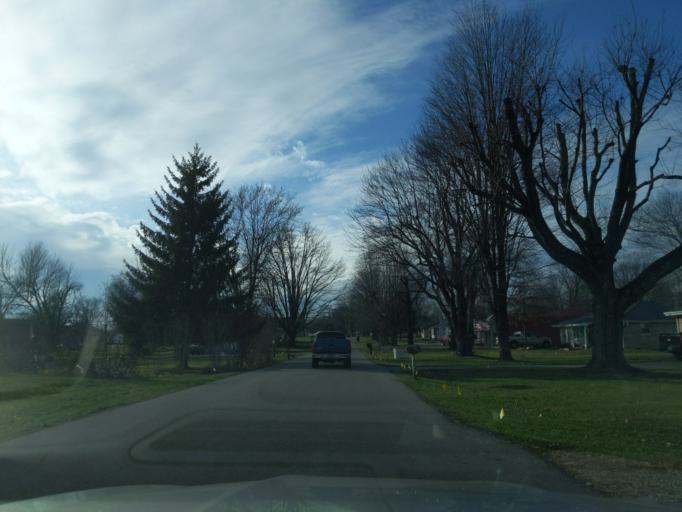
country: US
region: Indiana
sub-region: Decatur County
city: Westport
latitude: 39.1796
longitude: -85.5669
